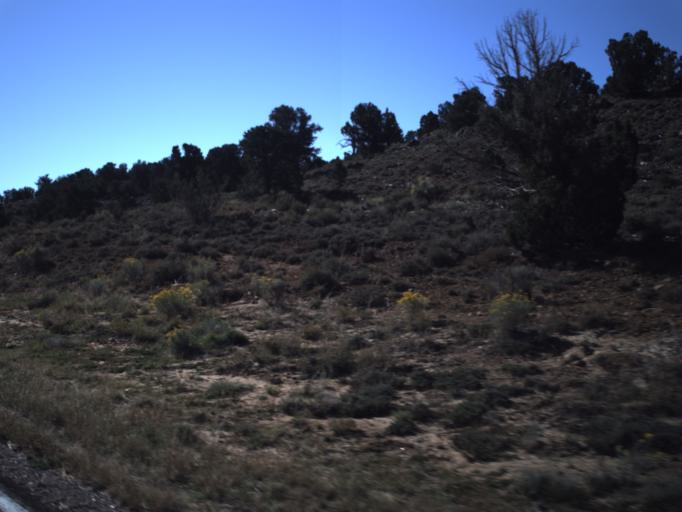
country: US
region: Utah
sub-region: Washington County
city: Enterprise
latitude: 37.6439
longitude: -113.4418
